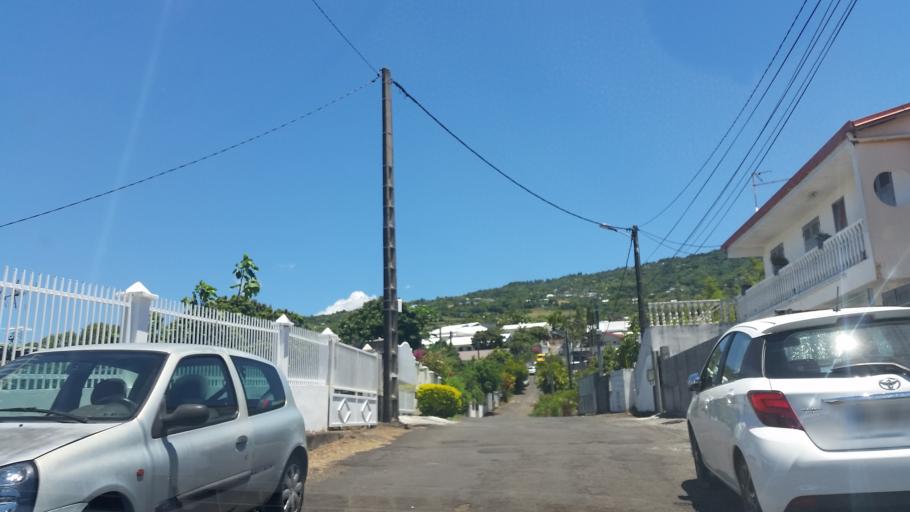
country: RE
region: Reunion
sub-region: Reunion
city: Sainte-Marie
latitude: -20.9317
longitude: 55.5311
